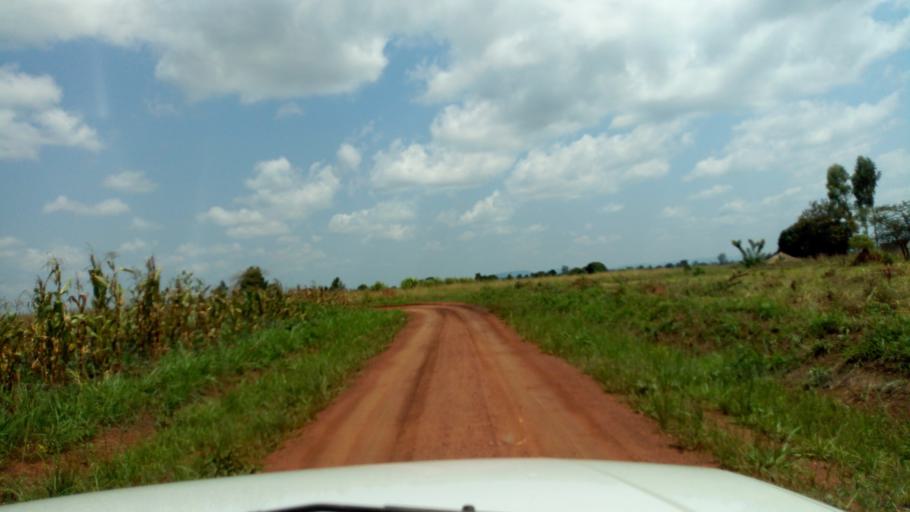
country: UG
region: Western Region
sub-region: Masindi District
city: Masindi
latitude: 1.7470
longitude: 31.8706
